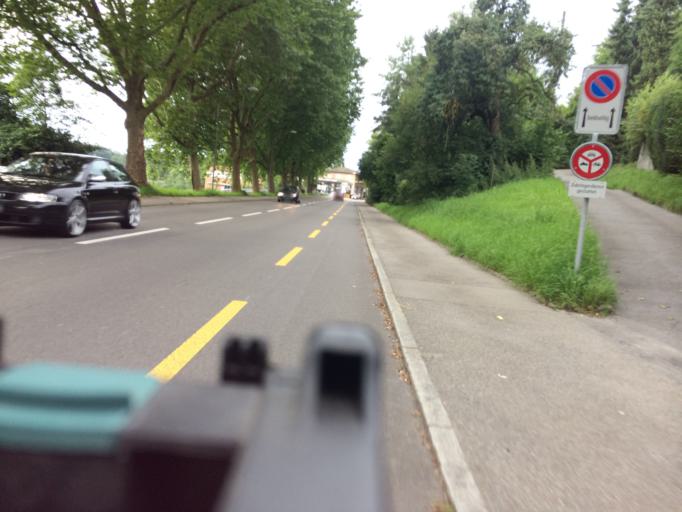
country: CH
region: Bern
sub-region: Bern-Mittelland District
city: Zollikofen
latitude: 46.9777
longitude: 7.4635
